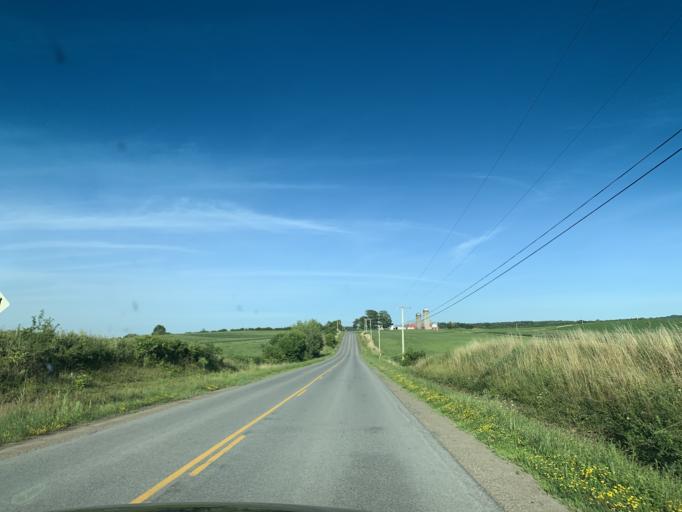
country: US
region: New York
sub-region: Oneida County
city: Vernon
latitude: 43.0559
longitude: -75.4836
